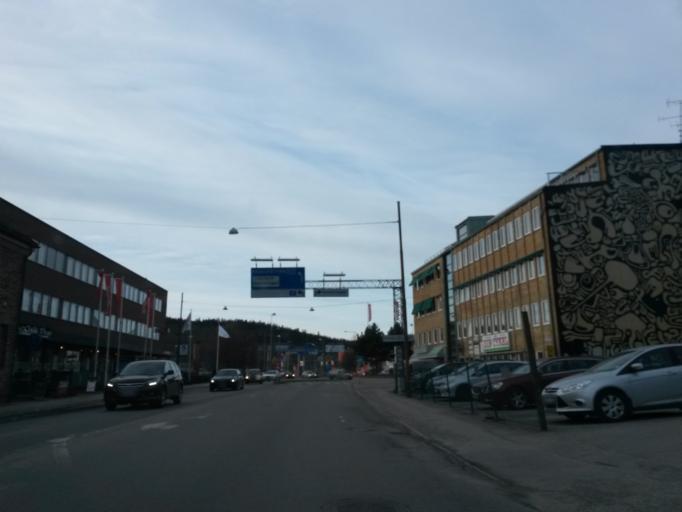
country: SE
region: Vaestra Goetaland
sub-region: Boras Kommun
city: Boras
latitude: 57.7309
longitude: 12.9391
